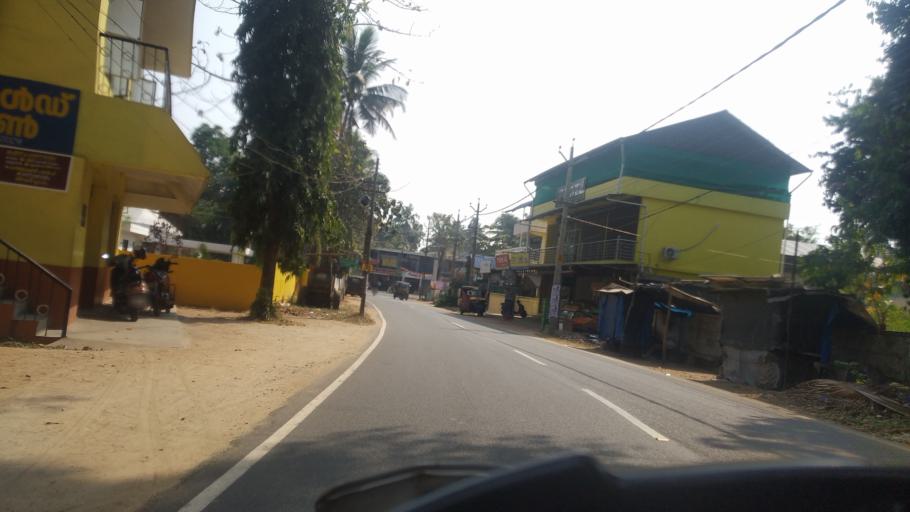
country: IN
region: Kerala
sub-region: Thrissur District
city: Kodungallur
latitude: 10.2078
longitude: 76.1854
